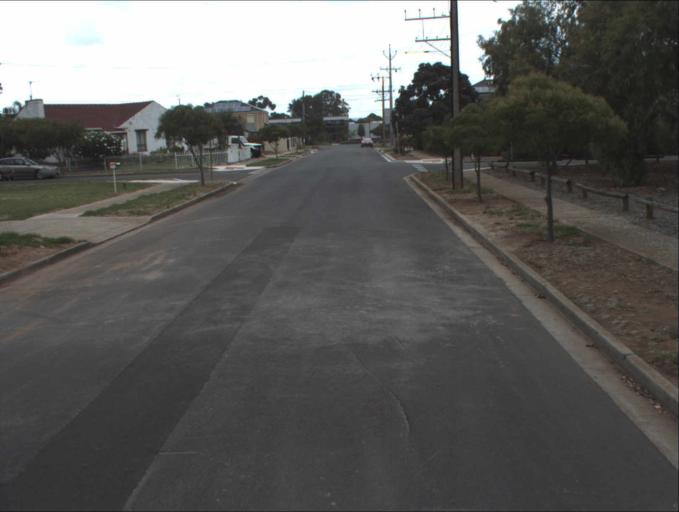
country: AU
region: South Australia
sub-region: Port Adelaide Enfield
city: Enfield
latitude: -34.8572
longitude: 138.6214
